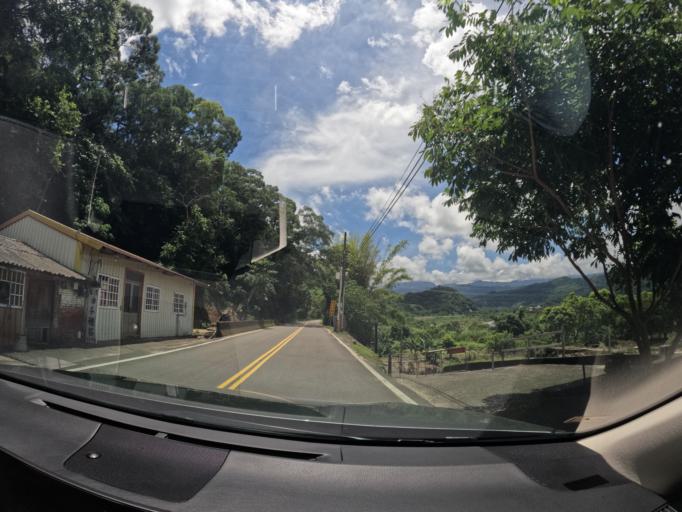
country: TW
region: Taiwan
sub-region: Hsinchu
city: Hsinchu
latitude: 24.6462
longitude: 120.9727
